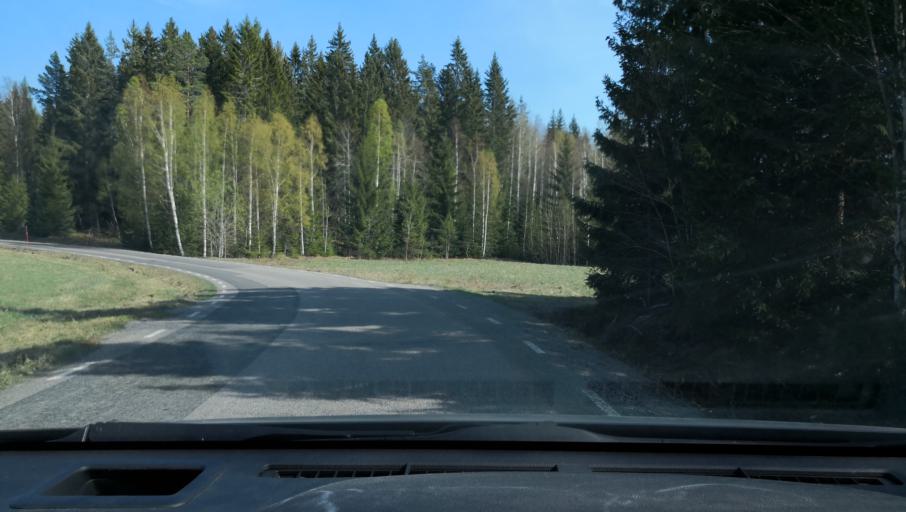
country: SE
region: Uppsala
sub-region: Heby Kommun
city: Heby
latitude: 60.0353
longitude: 16.8179
